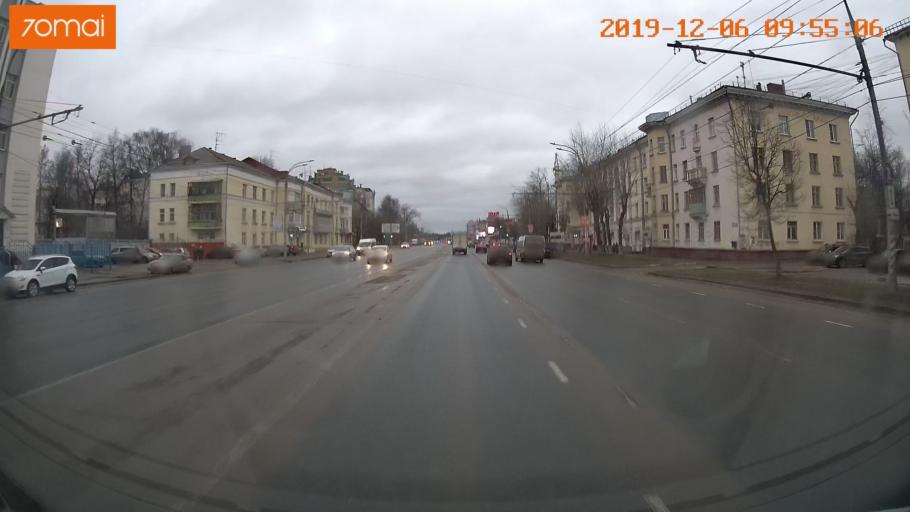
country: RU
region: Ivanovo
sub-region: Gorod Ivanovo
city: Ivanovo
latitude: 56.9781
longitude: 40.9772
